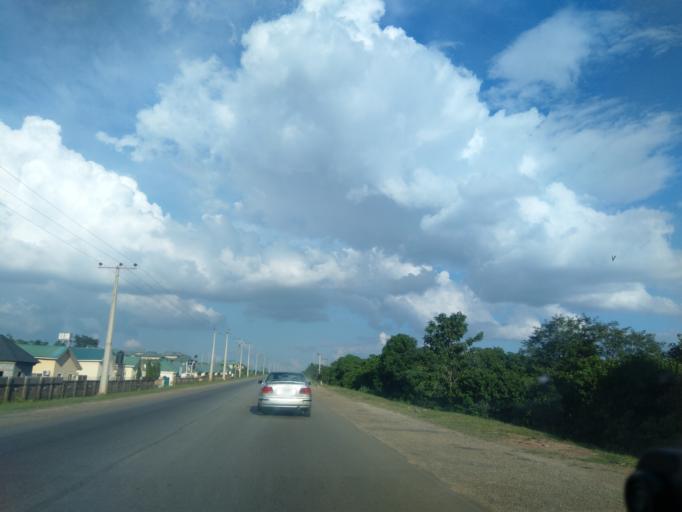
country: NG
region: Abuja Federal Capital Territory
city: Abuja
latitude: 9.0416
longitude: 7.3942
